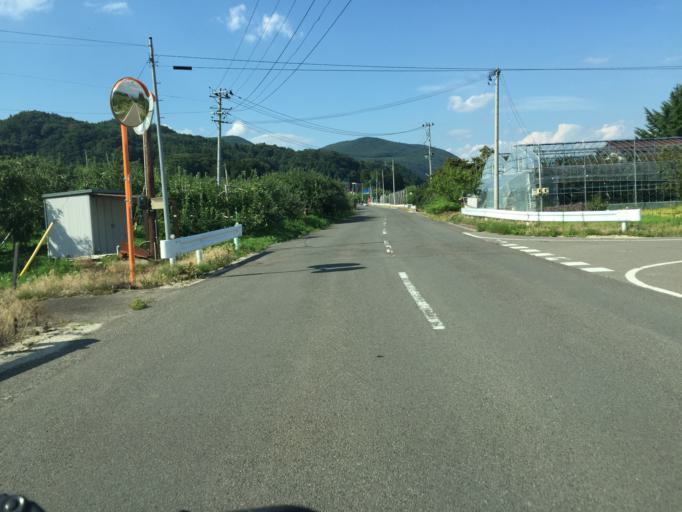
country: JP
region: Fukushima
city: Fukushima-shi
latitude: 37.7918
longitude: 140.3913
